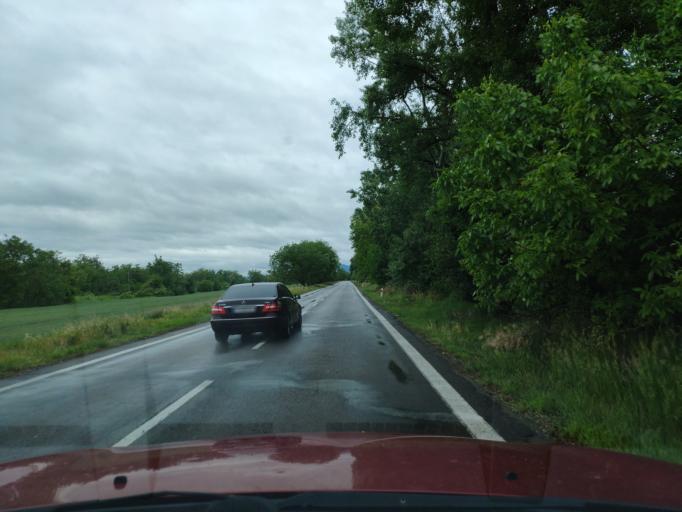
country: HU
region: Borsod-Abauj-Zemplen
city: Karcsa
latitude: 48.3898
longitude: 21.7864
